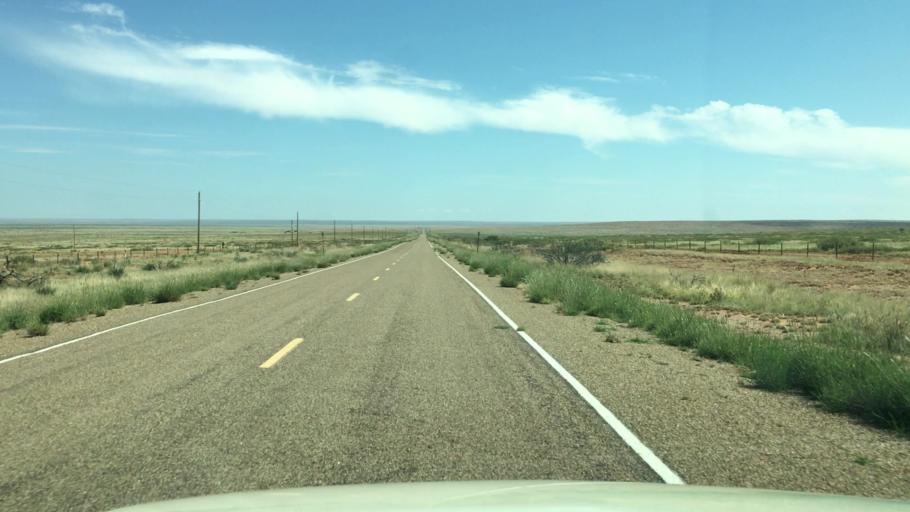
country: US
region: New Mexico
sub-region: De Baca County
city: Fort Sumner
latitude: 33.9855
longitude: -104.5727
